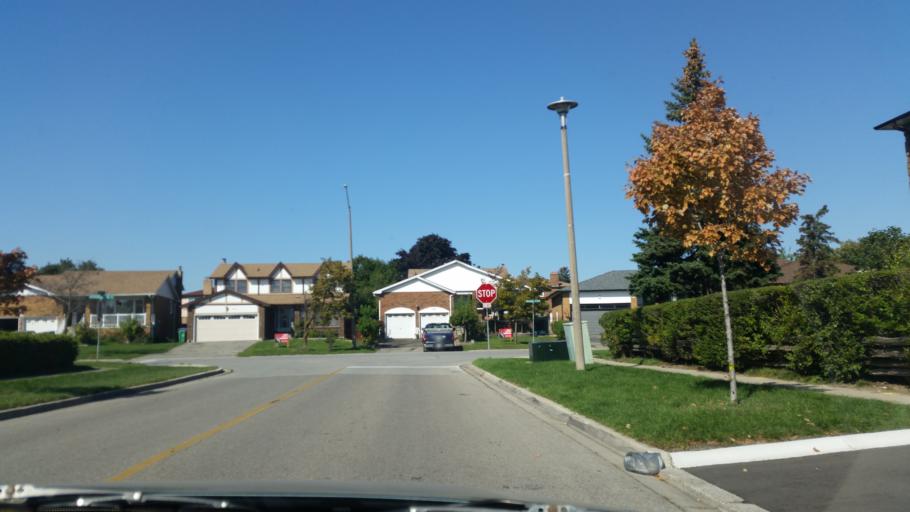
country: CA
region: Ontario
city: Brampton
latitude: 43.7132
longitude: -79.7686
